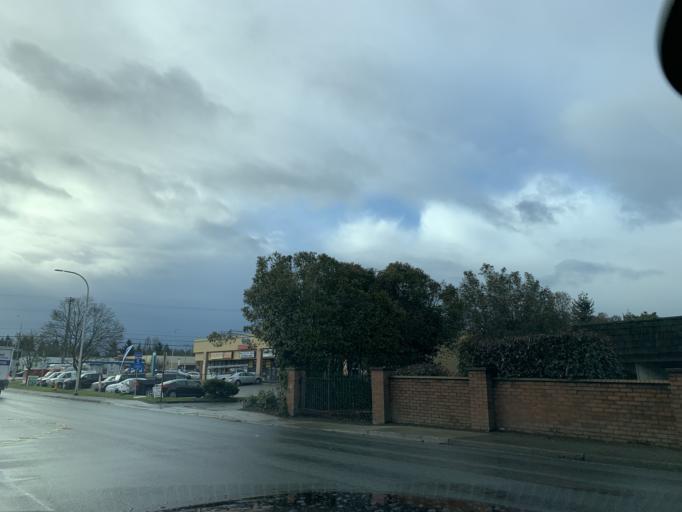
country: US
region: Washington
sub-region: Snohomish County
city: Martha Lake
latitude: 47.8831
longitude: -122.2388
